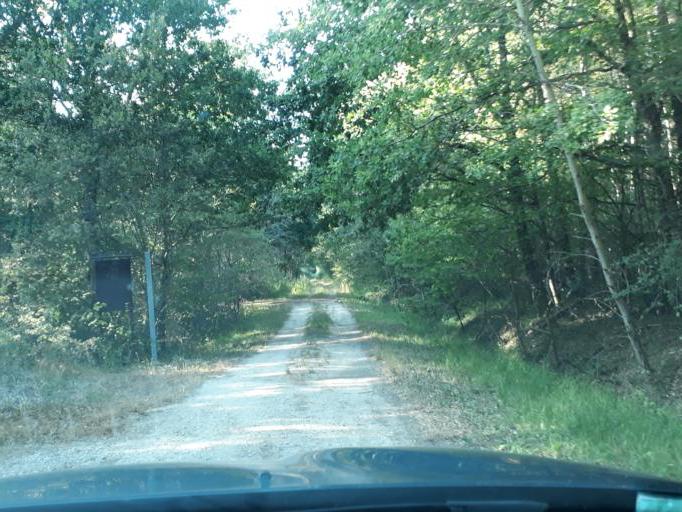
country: FR
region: Centre
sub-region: Departement du Loiret
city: Chaingy
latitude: 47.9138
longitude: 1.7415
